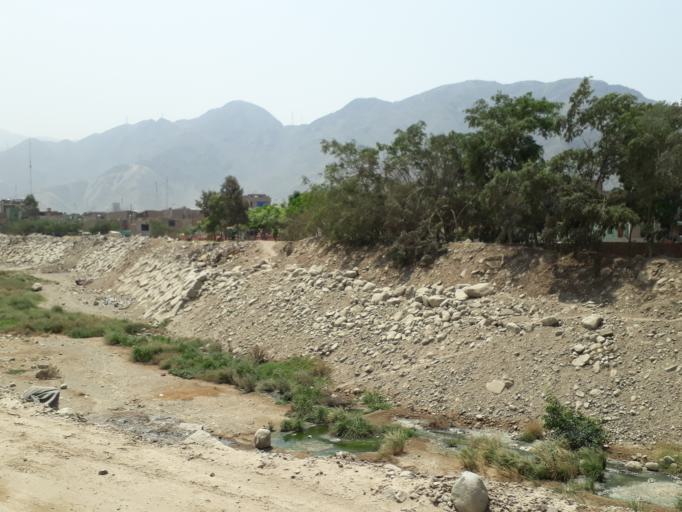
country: PE
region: Lima
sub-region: Lima
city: Santa Maria
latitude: -11.9885
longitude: -76.9023
